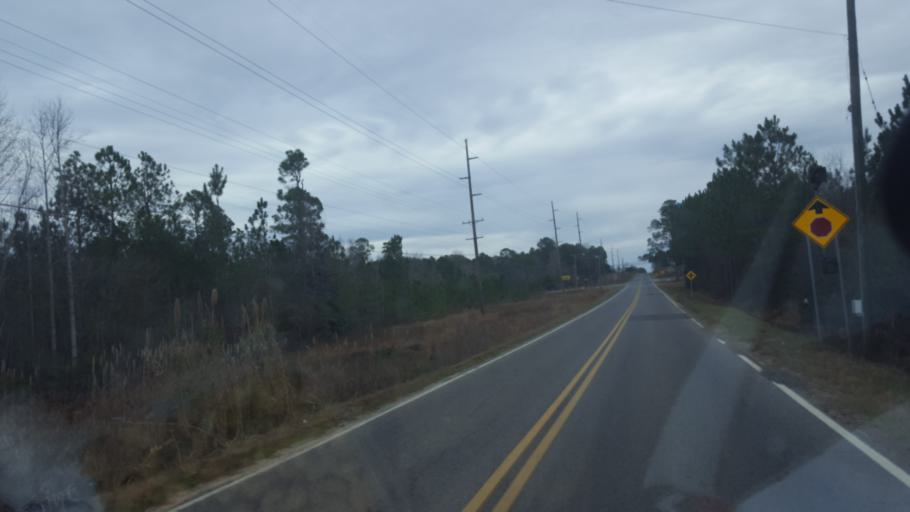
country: US
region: Georgia
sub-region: Ben Hill County
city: Fitzgerald
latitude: 31.7436
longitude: -83.2635
